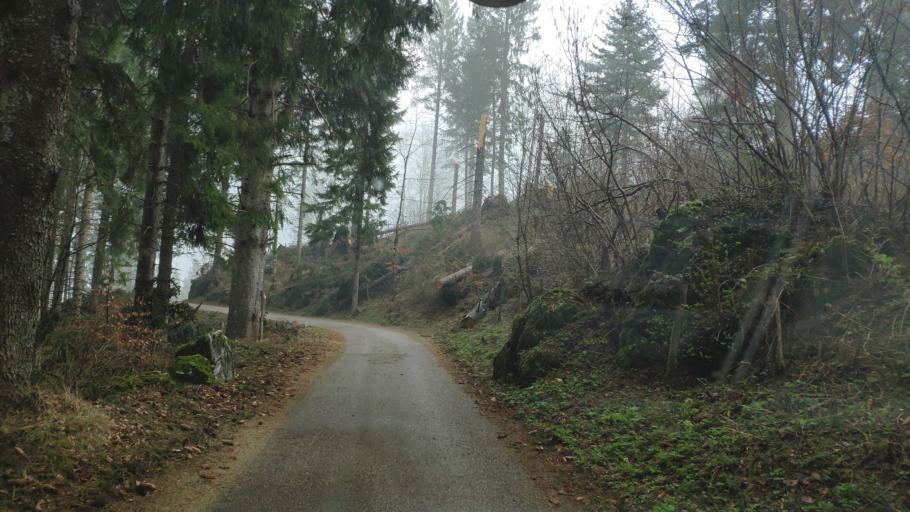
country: IT
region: Veneto
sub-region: Provincia di Vicenza
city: Rotzo
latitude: 45.8274
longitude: 11.4062
